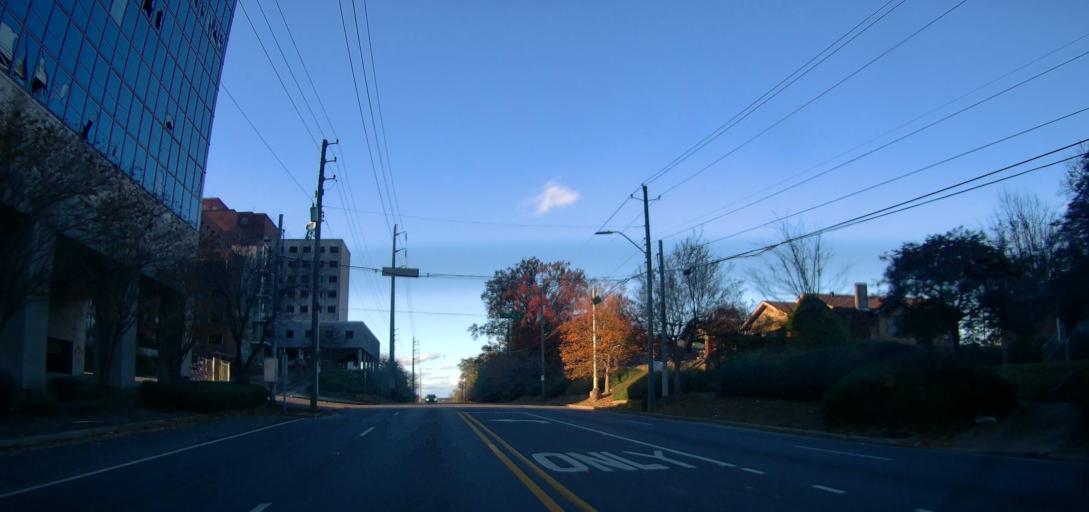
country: US
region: Alabama
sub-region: Jefferson County
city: Birmingham
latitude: 33.5360
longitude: -86.8094
